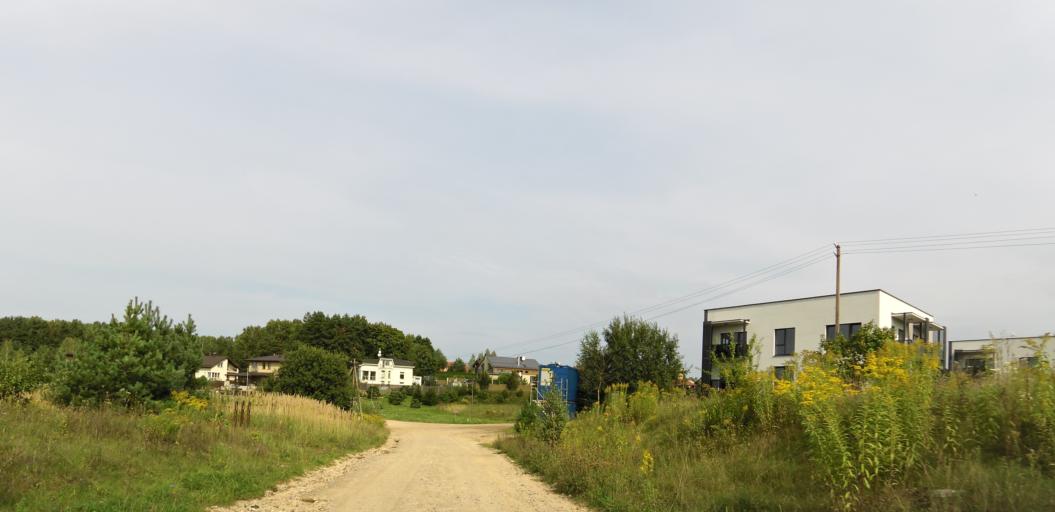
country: LT
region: Vilnius County
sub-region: Vilnius
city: Fabijoniskes
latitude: 54.7488
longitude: 25.2312
